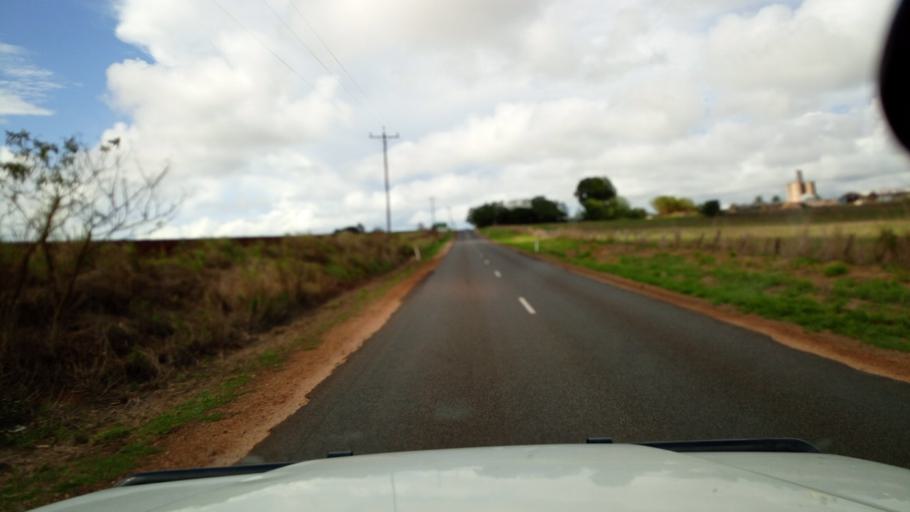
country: AU
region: Queensland
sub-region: Tablelands
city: Tolga
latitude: -17.2207
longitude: 145.5378
